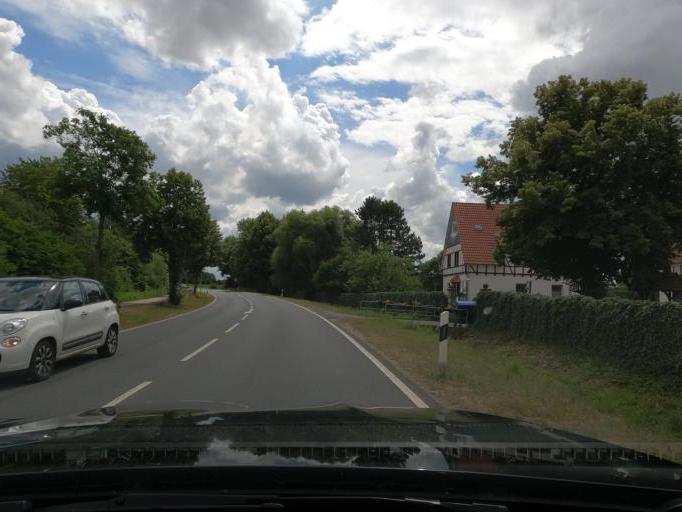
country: DE
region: Lower Saxony
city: Sehnde
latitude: 52.3385
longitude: 9.9317
